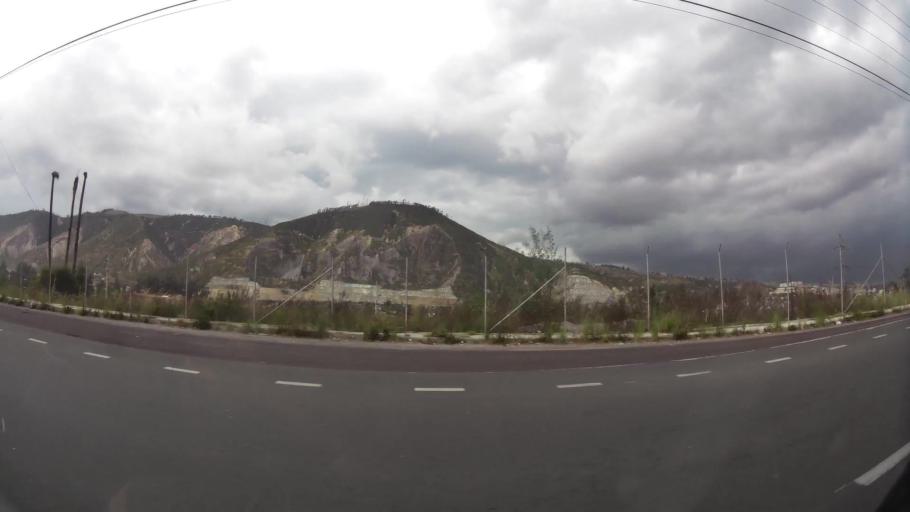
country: EC
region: Pichincha
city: Quito
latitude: -0.0482
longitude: -78.4560
